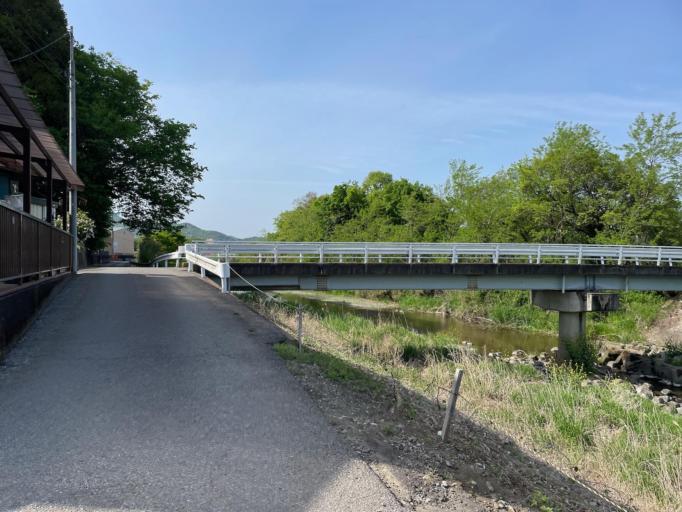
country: JP
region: Tochigi
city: Sano
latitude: 36.3085
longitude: 139.5371
